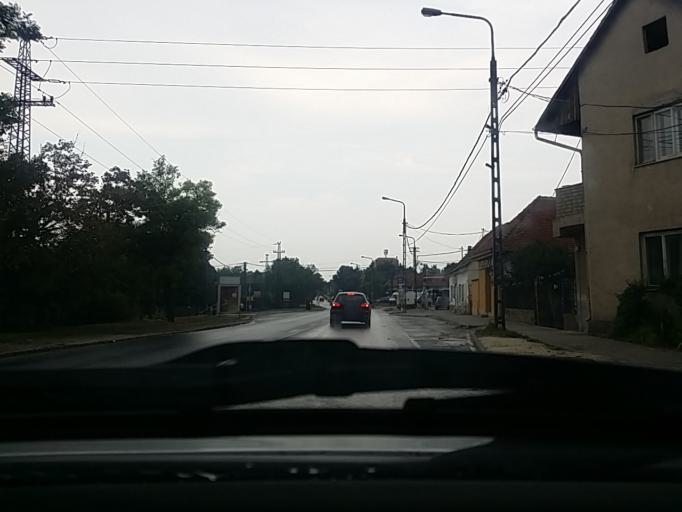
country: HU
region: Pest
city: Budakeszi
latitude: 47.5074
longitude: 18.9230
